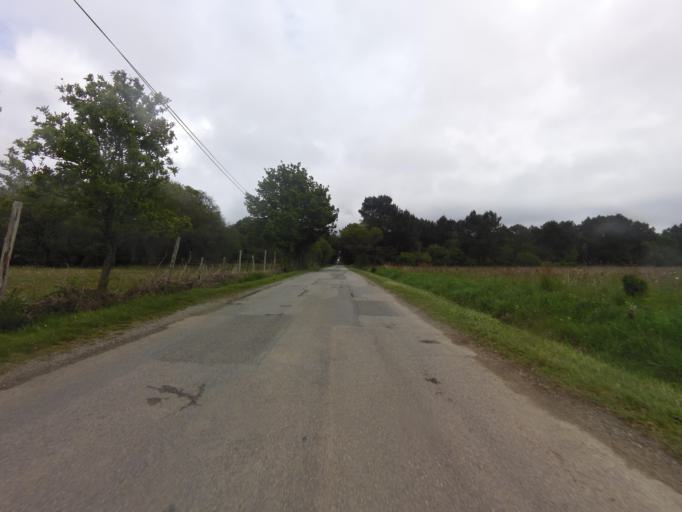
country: FR
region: Brittany
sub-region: Departement du Morbihan
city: Plougoumelen
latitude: 47.6358
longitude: -2.9064
